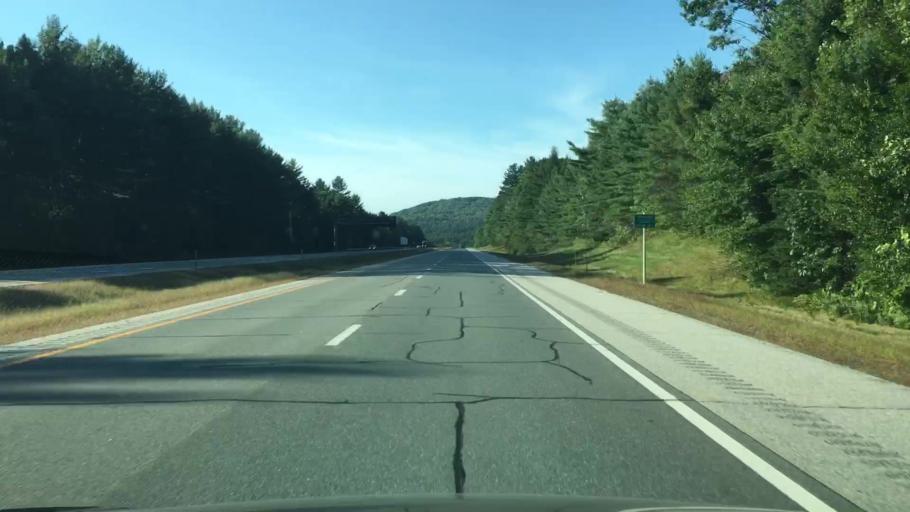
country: US
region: New Hampshire
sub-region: Grafton County
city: Littleton
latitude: 44.2369
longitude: -71.7553
